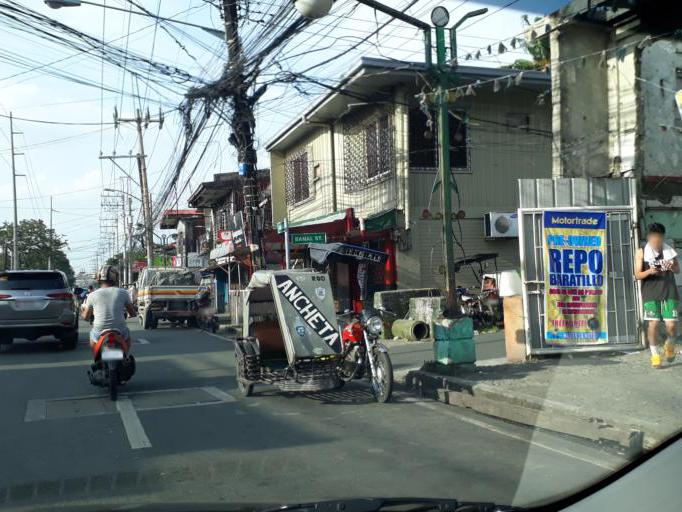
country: PH
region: Metro Manila
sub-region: City of Manila
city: Manila
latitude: 14.6311
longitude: 120.9745
